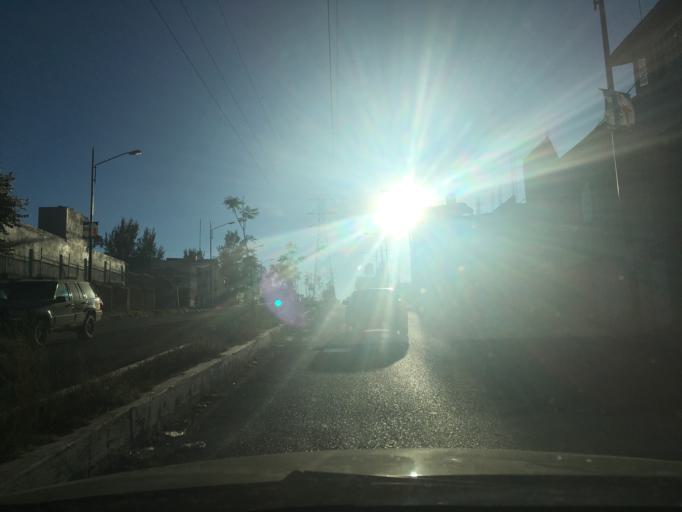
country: MX
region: Michoacan
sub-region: Morelia
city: Montana Monarca (Punta Altozano)
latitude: 19.6575
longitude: -101.1952
